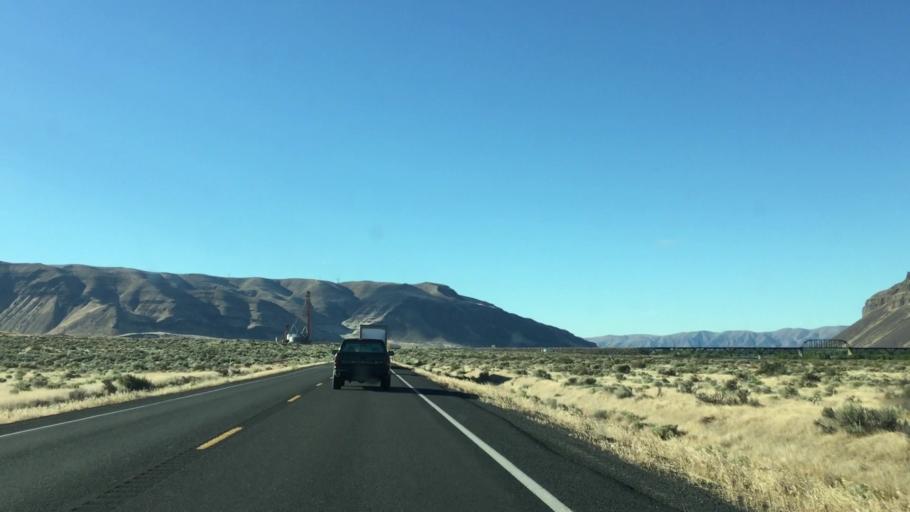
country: US
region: Washington
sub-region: Grant County
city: Mattawa
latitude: 46.8484
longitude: -119.9415
